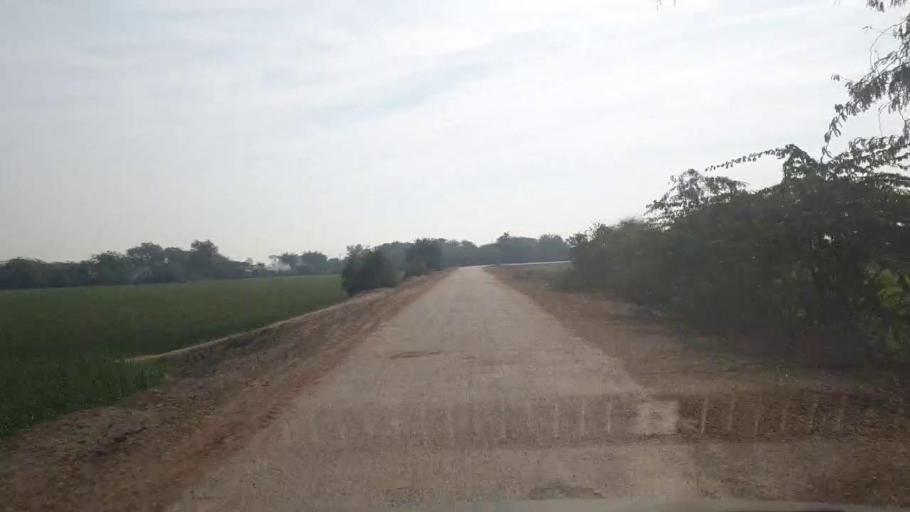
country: PK
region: Sindh
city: Shahpur Chakar
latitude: 26.1844
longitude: 68.5842
